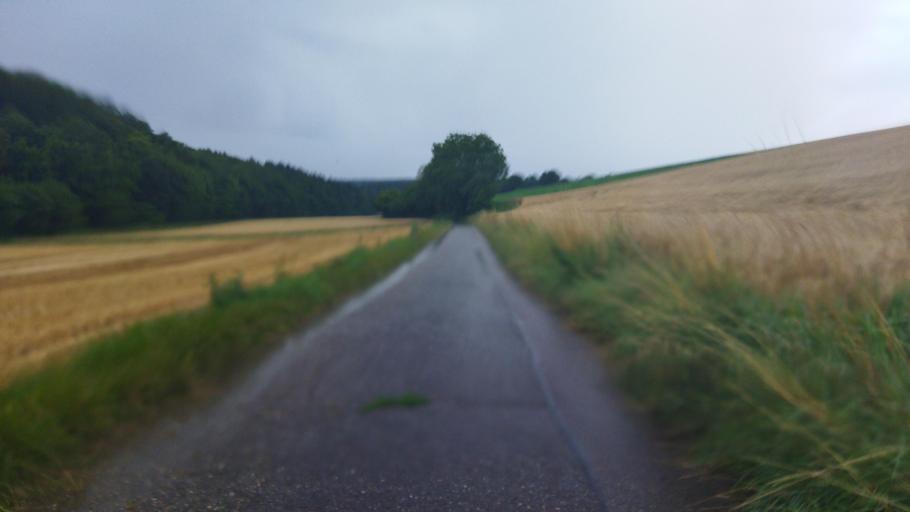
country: DE
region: Baden-Wuerttemberg
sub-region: Regierungsbezirk Stuttgart
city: Ittlingen
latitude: 49.2061
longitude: 8.9486
